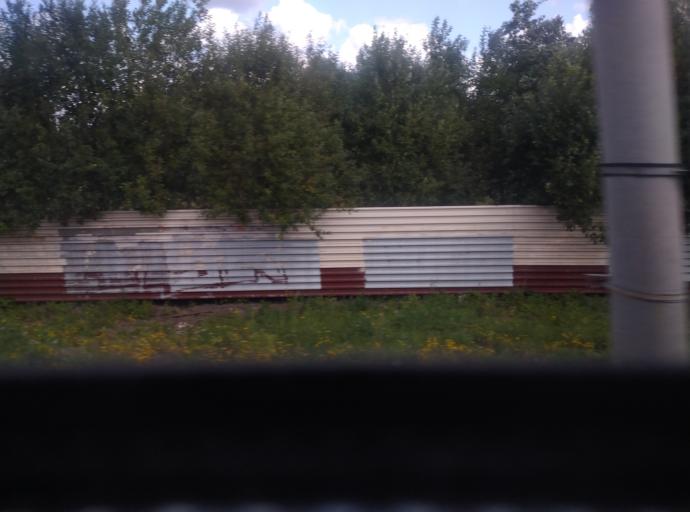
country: RU
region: St.-Petersburg
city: Kolpino
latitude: 59.7572
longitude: 30.5996
